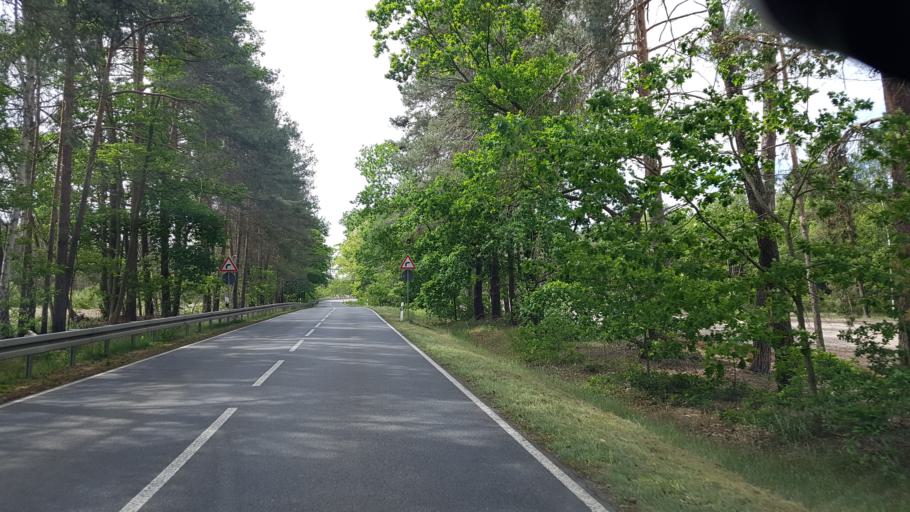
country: DE
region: Brandenburg
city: Sonnewalde
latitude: 51.7619
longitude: 13.6857
